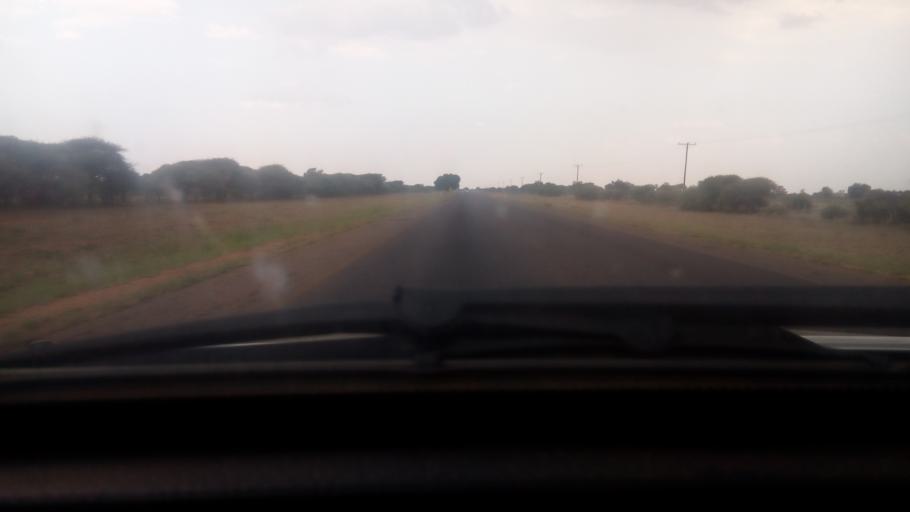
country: BW
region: Kweneng
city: Metsemotlhaba
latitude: -24.4732
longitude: 25.7041
